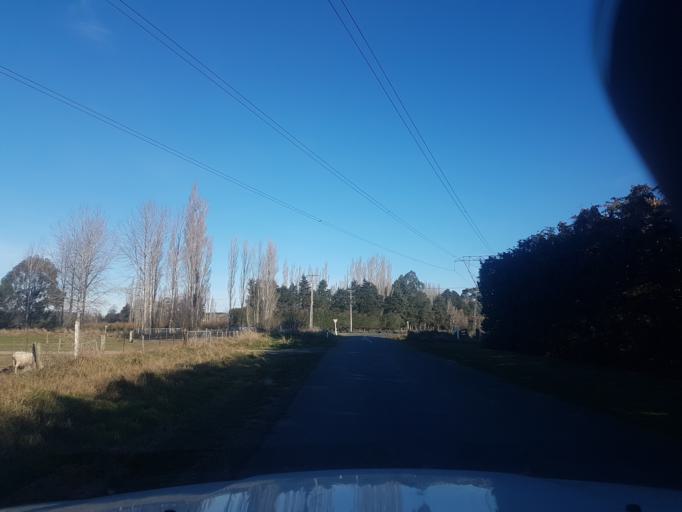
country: NZ
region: Canterbury
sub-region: Timaru District
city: Pleasant Point
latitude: -44.2772
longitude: 171.1705
